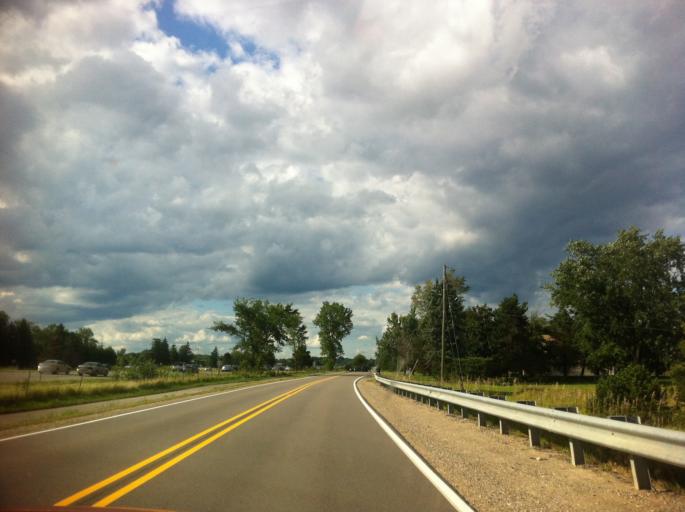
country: US
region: Michigan
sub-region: Livingston County
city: Whitmore Lake
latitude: 42.4853
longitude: -83.7567
